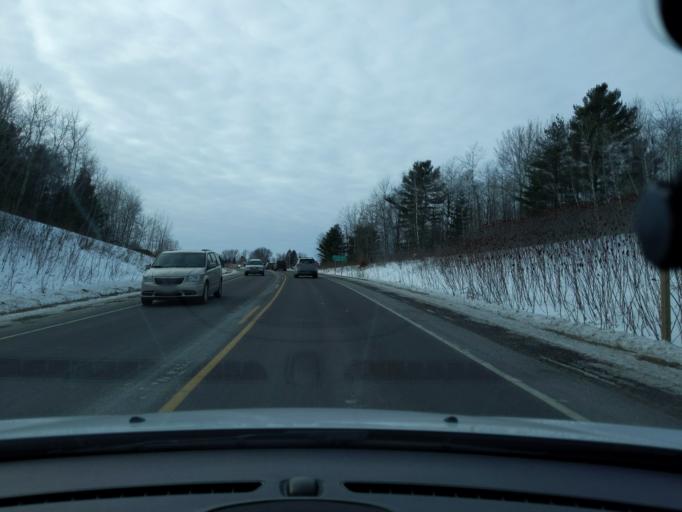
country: US
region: Wisconsin
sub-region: Polk County
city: Clear Lake
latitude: 45.2535
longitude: -92.2797
